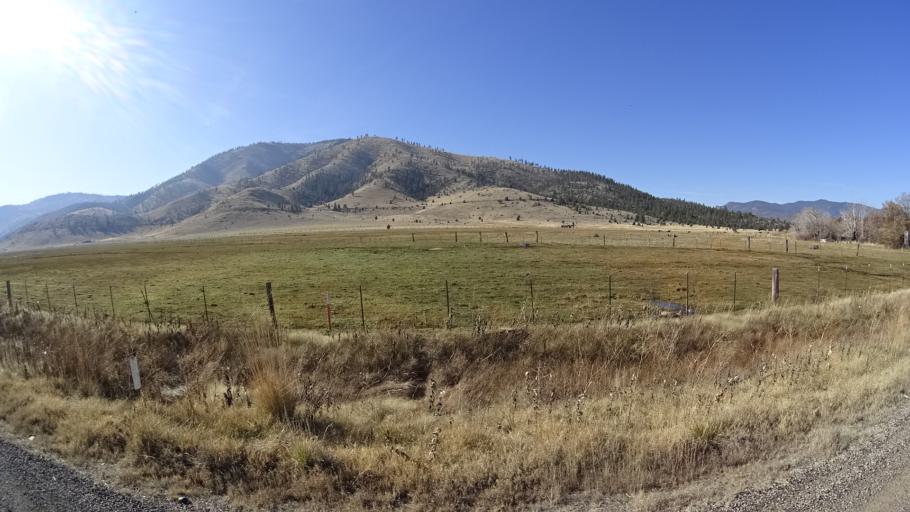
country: US
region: California
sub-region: Siskiyou County
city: Weed
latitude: 41.4899
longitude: -122.5058
